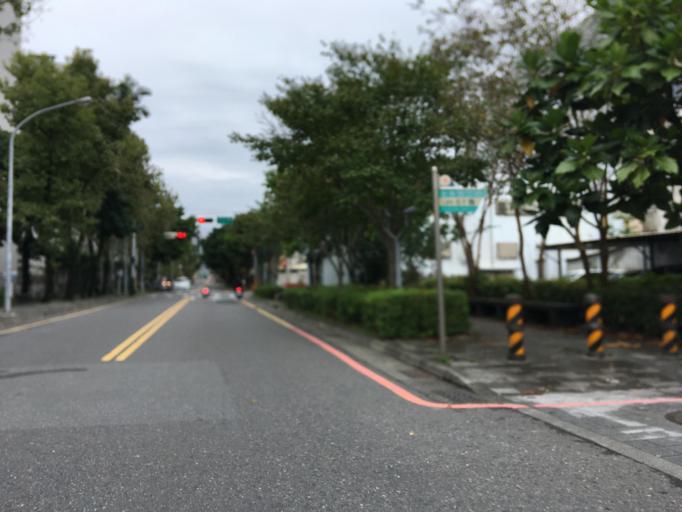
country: TW
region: Taiwan
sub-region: Yilan
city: Yilan
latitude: 24.7473
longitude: 121.7479
